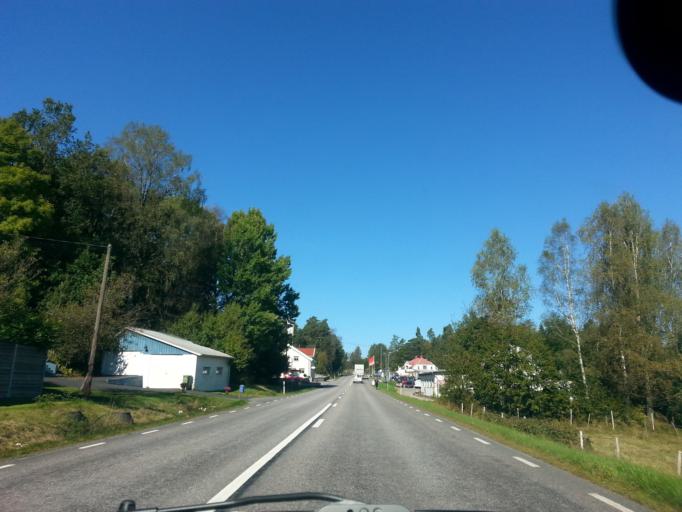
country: SE
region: Vaestra Goetaland
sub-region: Harryda Kommun
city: Ravlanda
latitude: 57.5474
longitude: 12.5332
